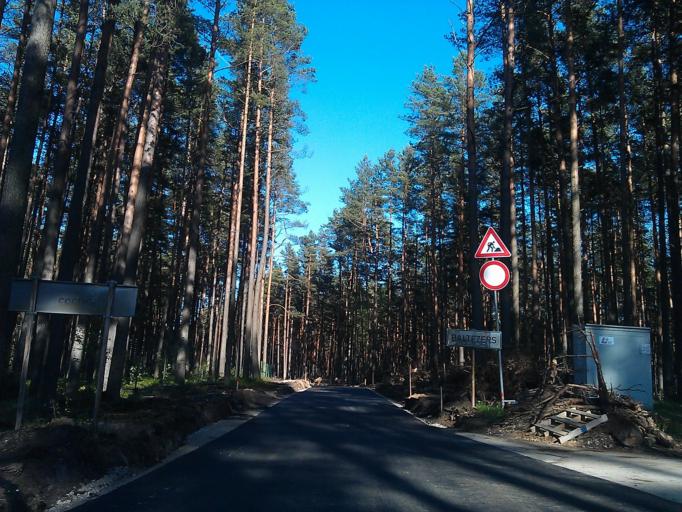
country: LV
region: Riga
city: Bergi
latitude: 57.0155
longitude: 24.2919
